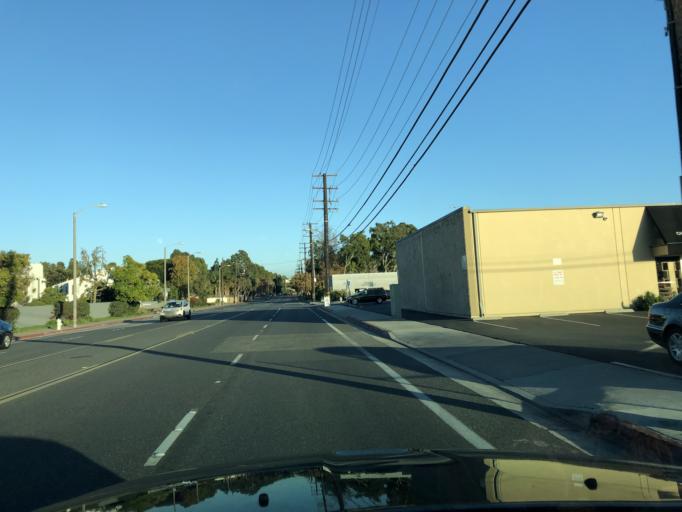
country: US
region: California
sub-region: Orange County
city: Costa Mesa
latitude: 33.6822
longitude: -117.8834
